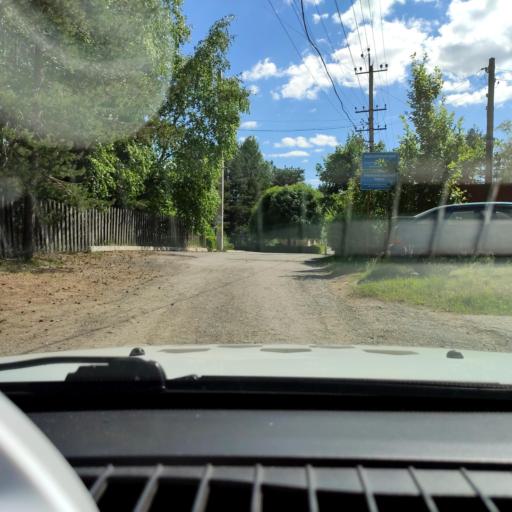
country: RU
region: Perm
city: Perm
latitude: 58.0612
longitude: 56.3075
